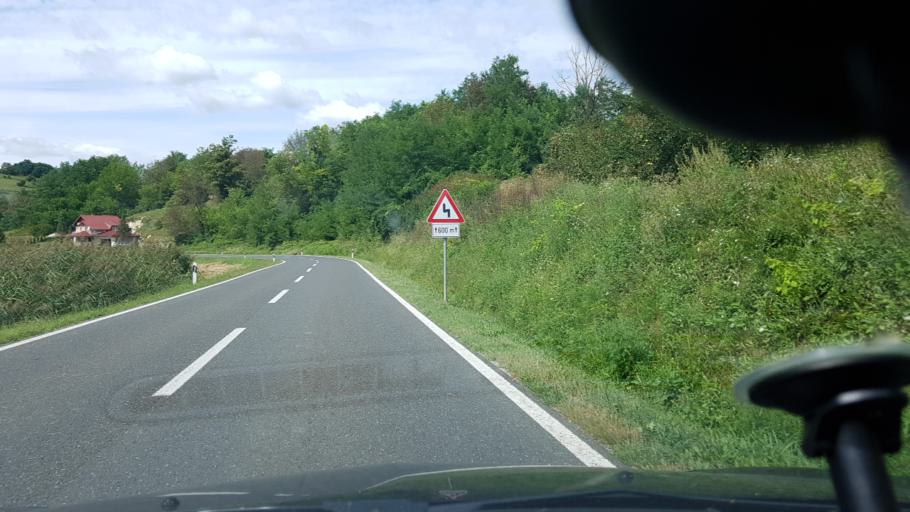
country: HR
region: Varazdinska
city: Lepoglava
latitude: 46.2150
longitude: 16.0081
